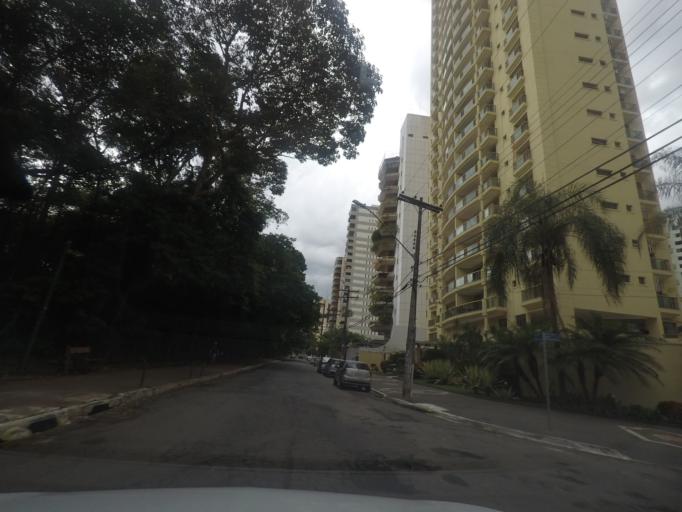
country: BR
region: Goias
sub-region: Goiania
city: Goiania
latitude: -16.6806
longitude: -49.2636
